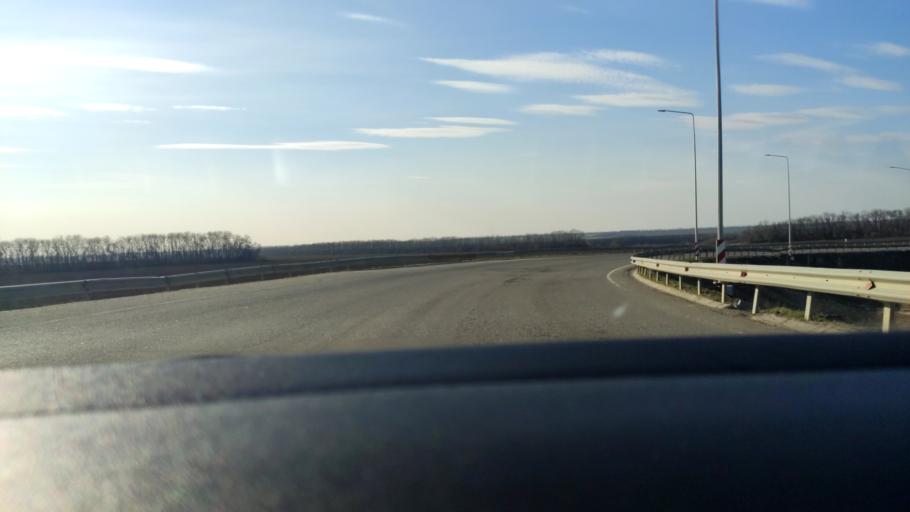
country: RU
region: Voronezj
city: Kolodeznyy
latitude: 51.3395
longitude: 39.0217
